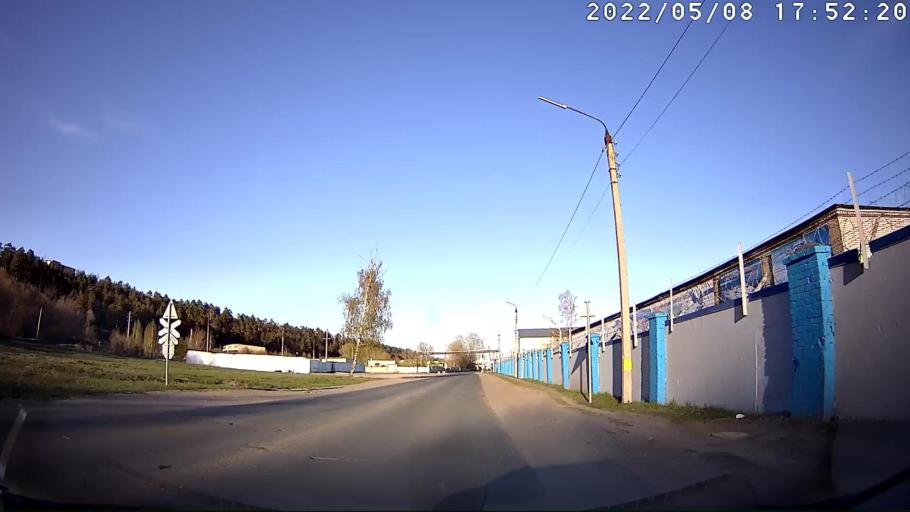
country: RU
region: Tatarstan
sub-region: Zelenodol'skiy Rayon
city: Zelenodolsk
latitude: 55.8408
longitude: 48.5033
